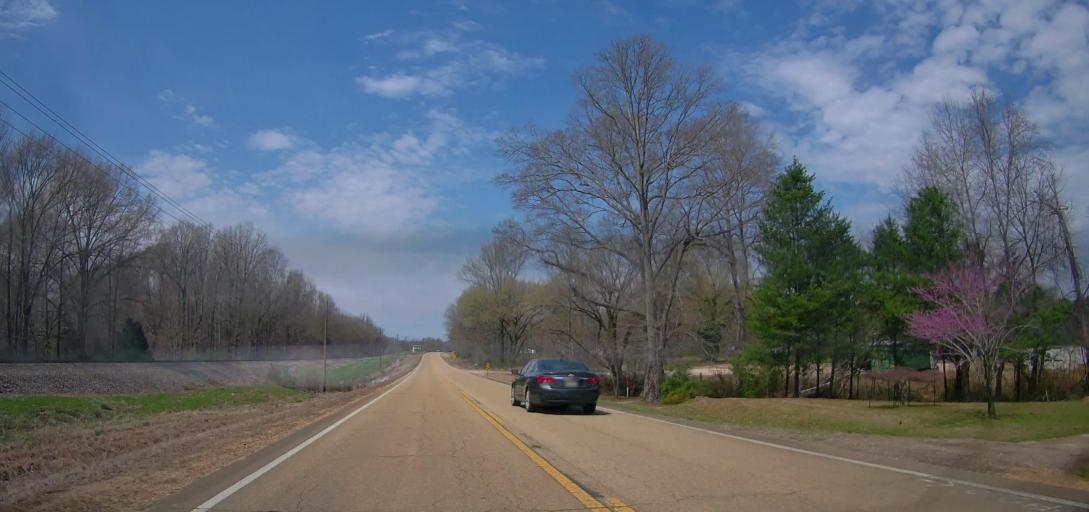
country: US
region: Mississippi
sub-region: Benton County
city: Ashland
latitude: 34.6289
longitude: -89.2667
